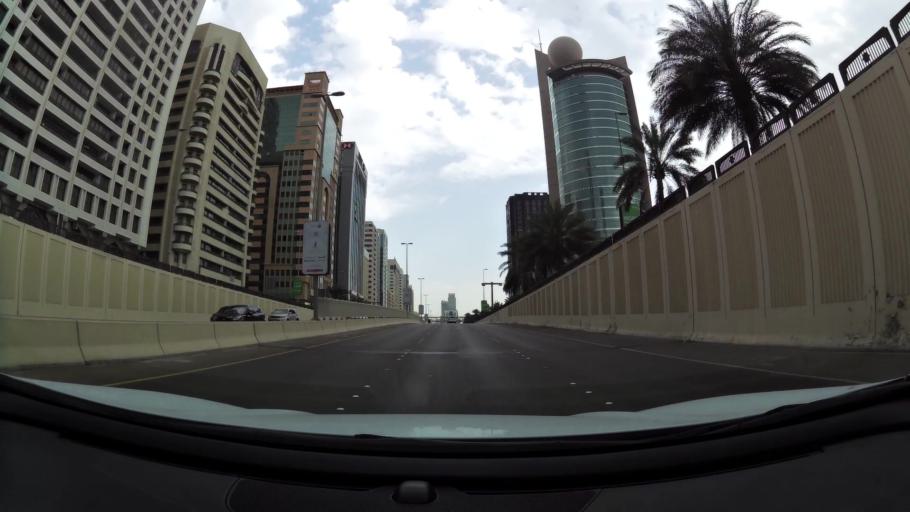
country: AE
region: Abu Dhabi
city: Abu Dhabi
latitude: 24.4818
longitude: 54.3599
